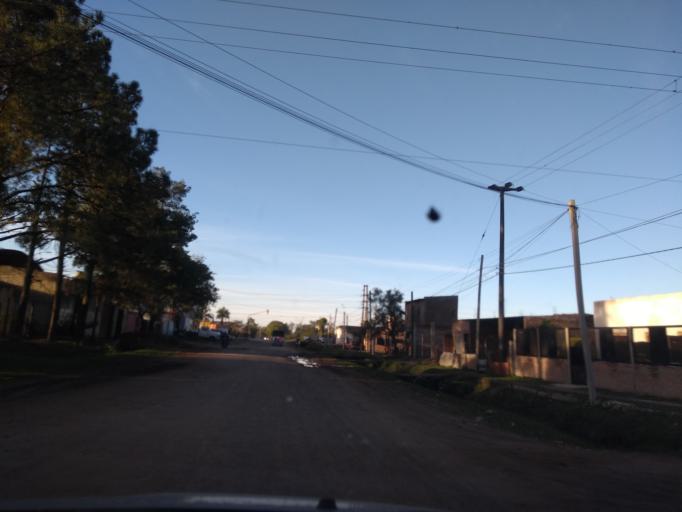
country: AR
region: Chaco
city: Resistencia
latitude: -27.4839
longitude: -58.9658
